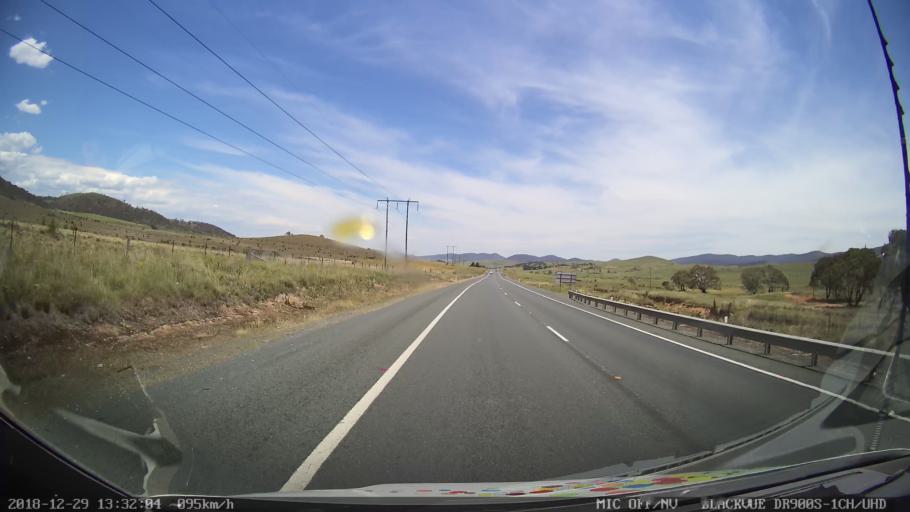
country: AU
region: New South Wales
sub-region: Cooma-Monaro
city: Cooma
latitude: -35.9255
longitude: 149.1512
